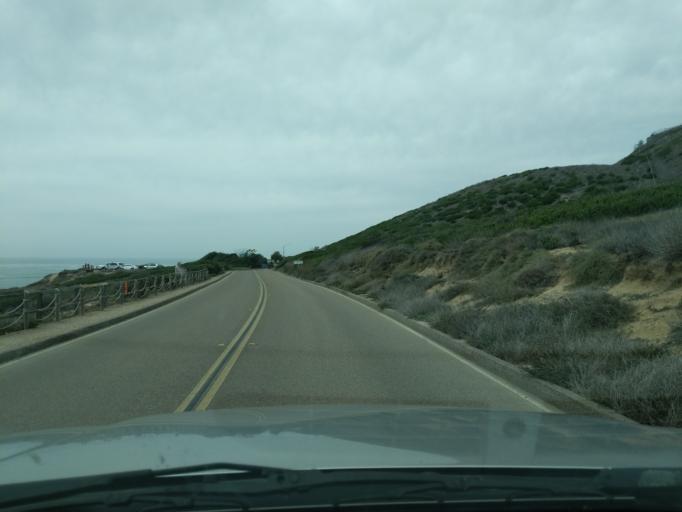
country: US
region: California
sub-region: San Diego County
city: Coronado
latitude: 32.6742
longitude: -117.2450
